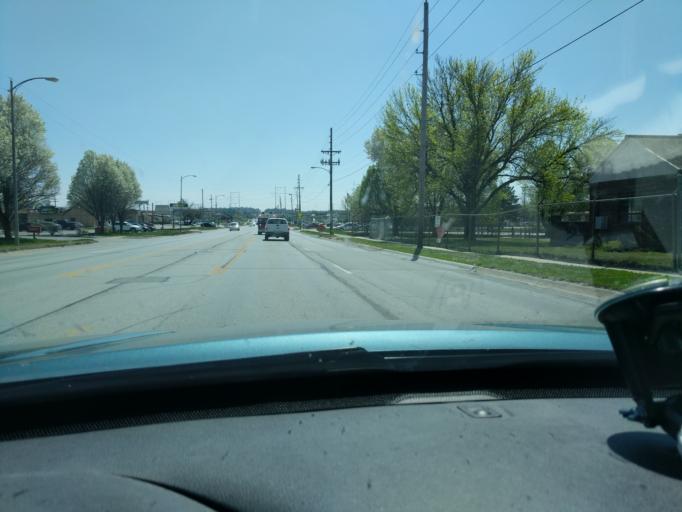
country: US
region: Nebraska
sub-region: Douglas County
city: Ralston
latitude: 41.2324
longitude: -96.0431
